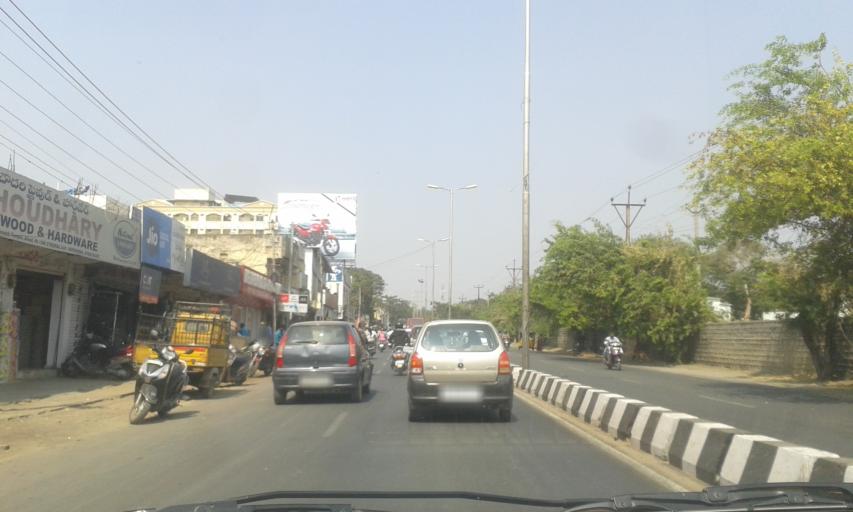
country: IN
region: Telangana
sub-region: Rangareddi
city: Secunderabad
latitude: 17.4978
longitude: 78.5133
